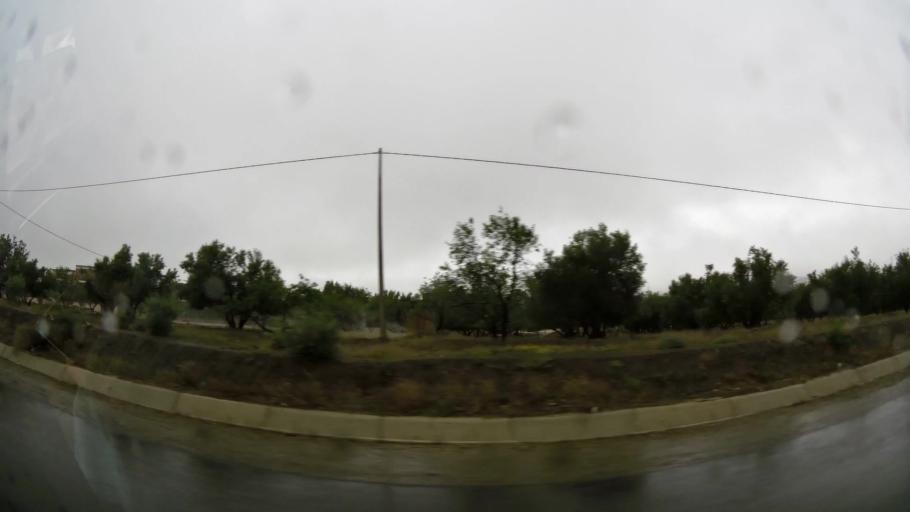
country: MA
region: Oriental
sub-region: Nador
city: Midar
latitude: 34.8491
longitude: -3.7217
